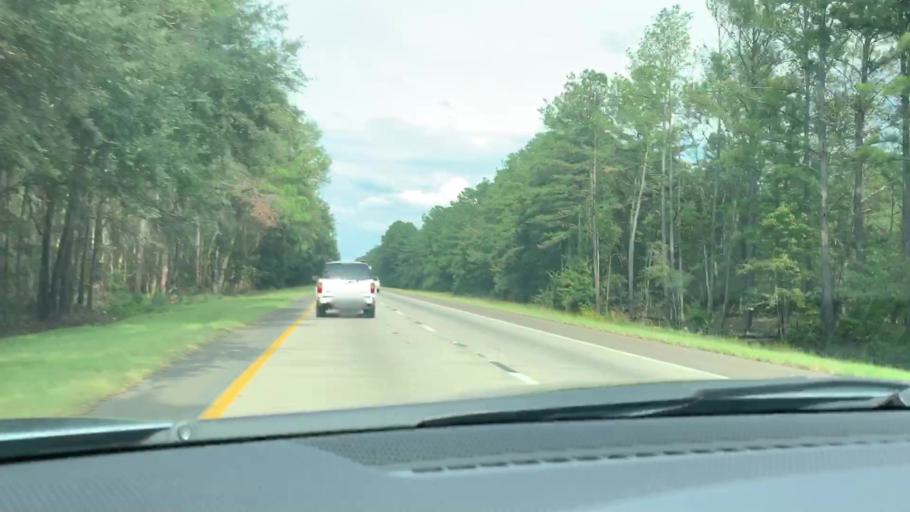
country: US
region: South Carolina
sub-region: Hampton County
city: Yemassee
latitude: 32.7622
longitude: -80.8147
